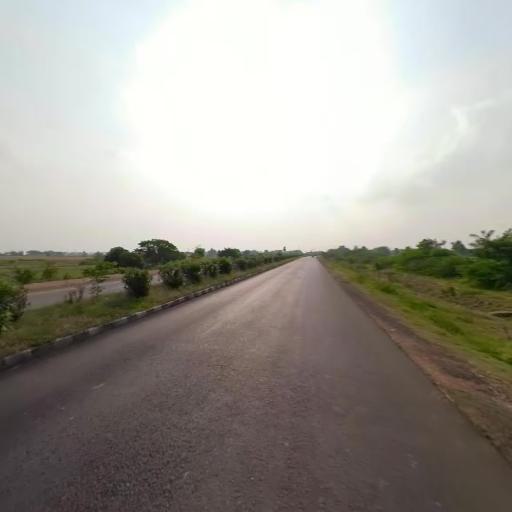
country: IN
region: Telangana
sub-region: Nalgonda
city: Suriapet
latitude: 17.1703
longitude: 79.5043
